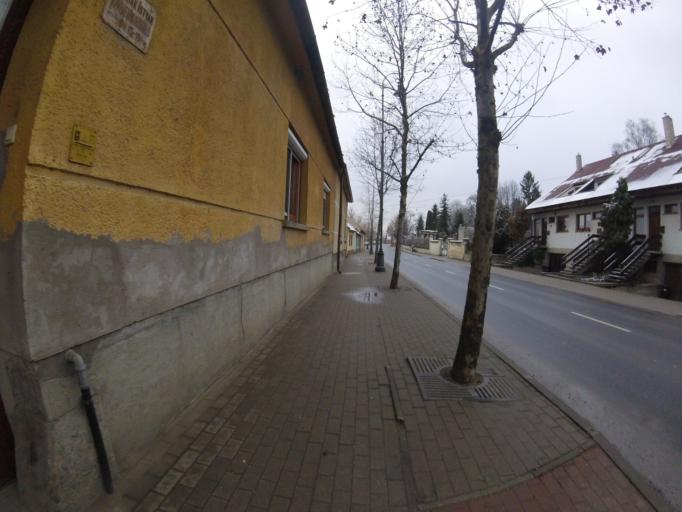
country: HU
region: Komarom-Esztergom
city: Esztergom
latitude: 47.7866
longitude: 18.7465
